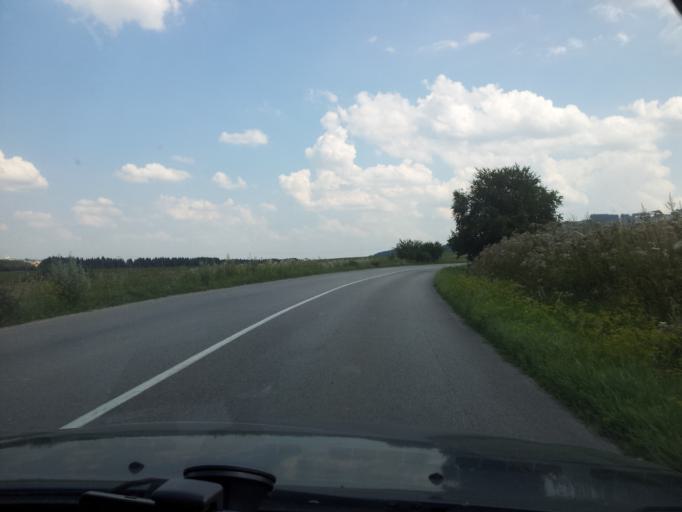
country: SK
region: Zilinsky
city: Namestovo
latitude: 49.3895
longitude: 19.4552
